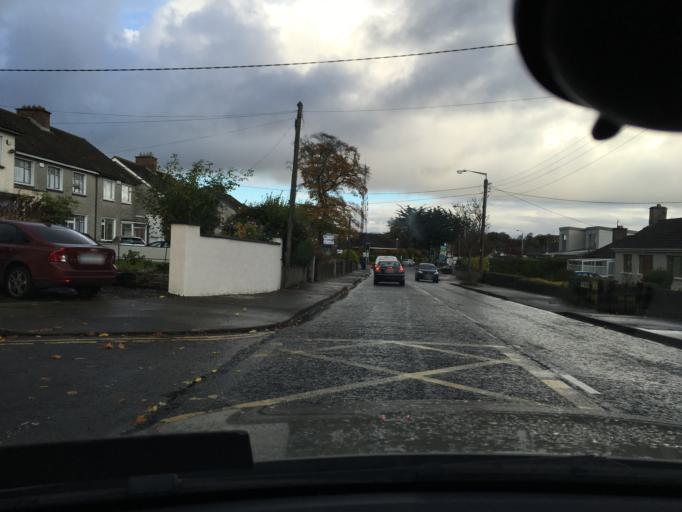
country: IE
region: Leinster
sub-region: Fingal County
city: Blanchardstown
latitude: 53.3881
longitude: -6.3827
